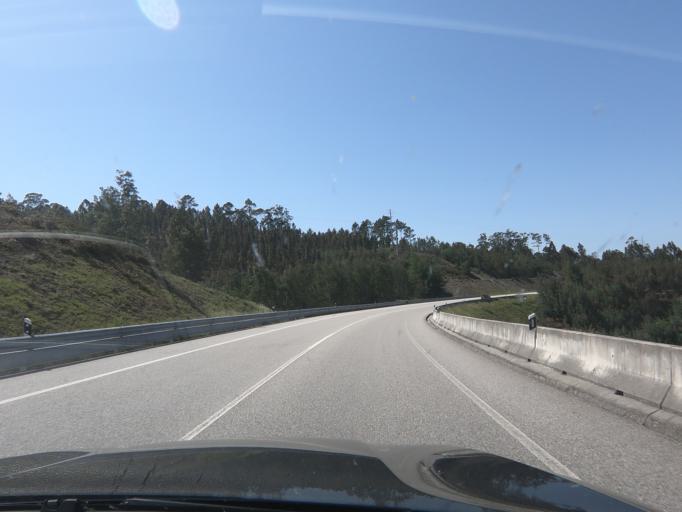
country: PT
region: Coimbra
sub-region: Lousa
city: Lousa
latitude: 40.1504
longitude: -8.2627
